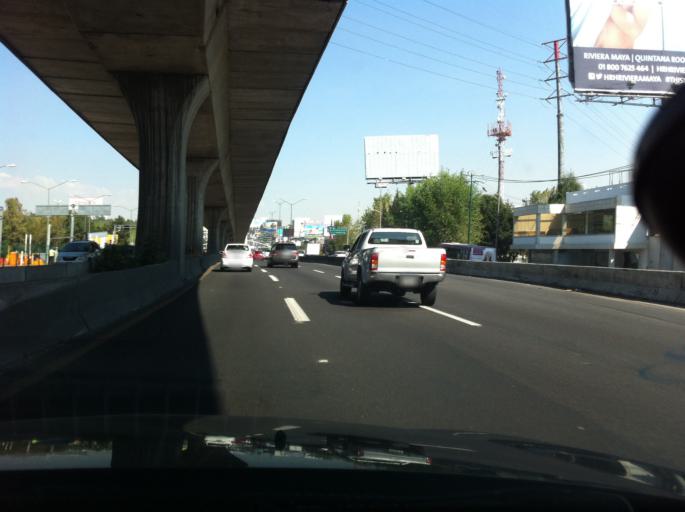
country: MX
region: Mexico
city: Naucalpan de Juarez
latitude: 19.4903
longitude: -99.2370
